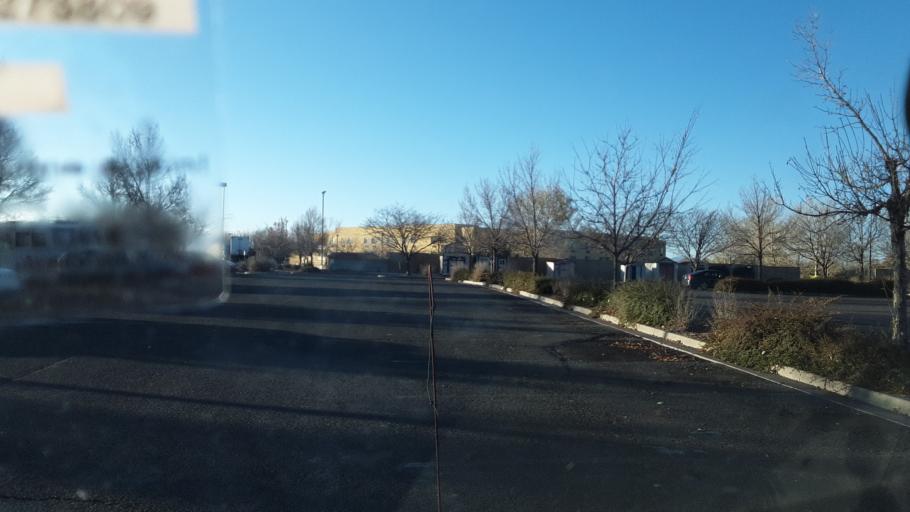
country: US
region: New Mexico
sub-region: Santa Fe County
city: Agua Fria
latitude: 35.6515
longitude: -106.0027
